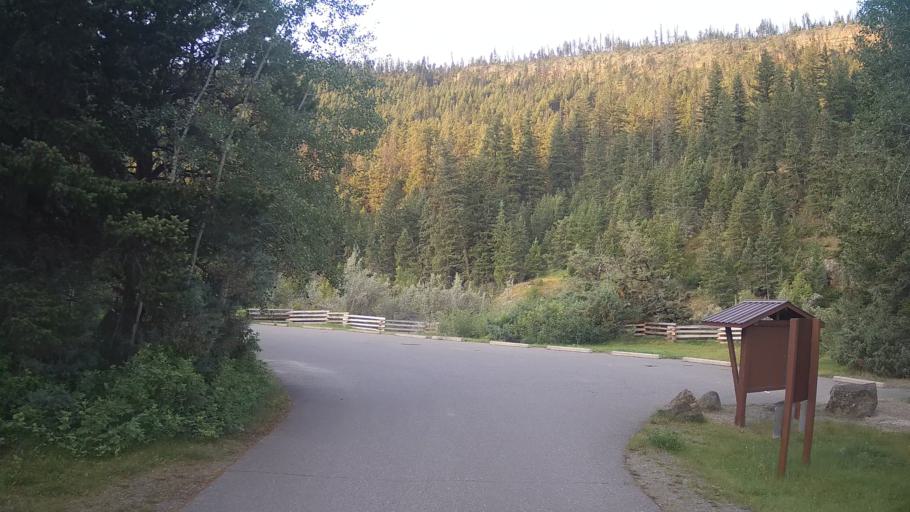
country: CA
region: British Columbia
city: Hanceville
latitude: 52.0878
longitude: -123.3961
